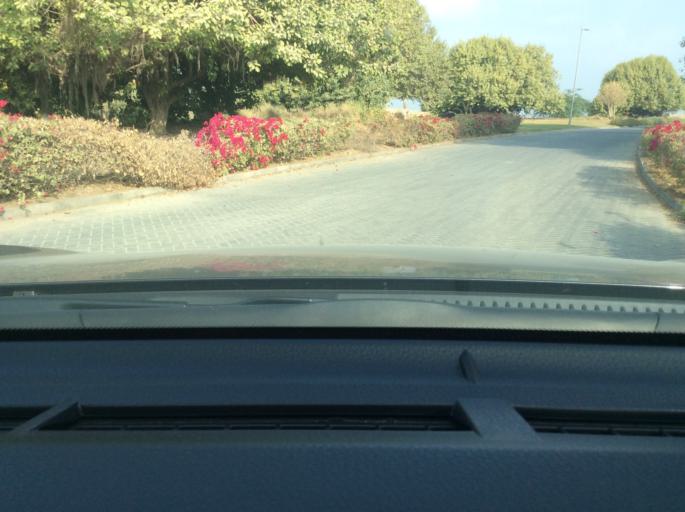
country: OM
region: Muhafazat Masqat
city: As Sib al Jadidah
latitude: 23.6286
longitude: 58.2620
